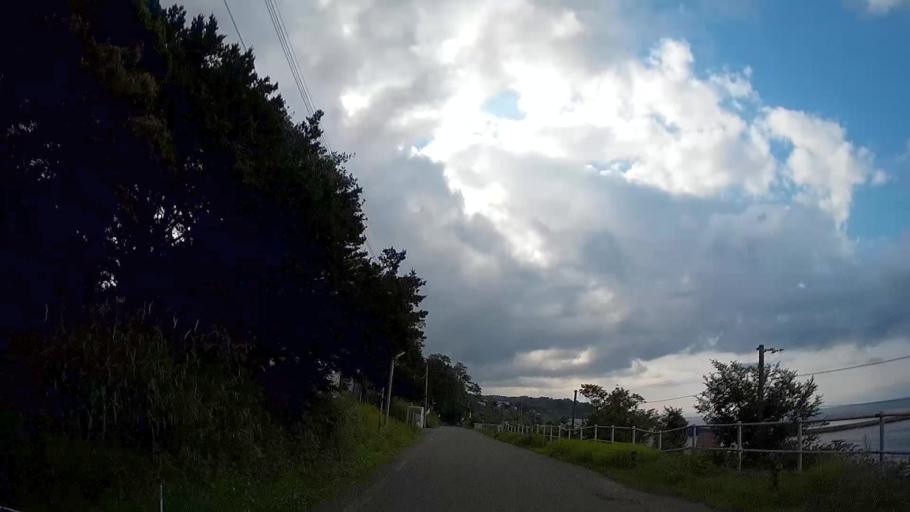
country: JP
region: Hokkaido
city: Nanae
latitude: 42.1131
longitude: 140.5482
